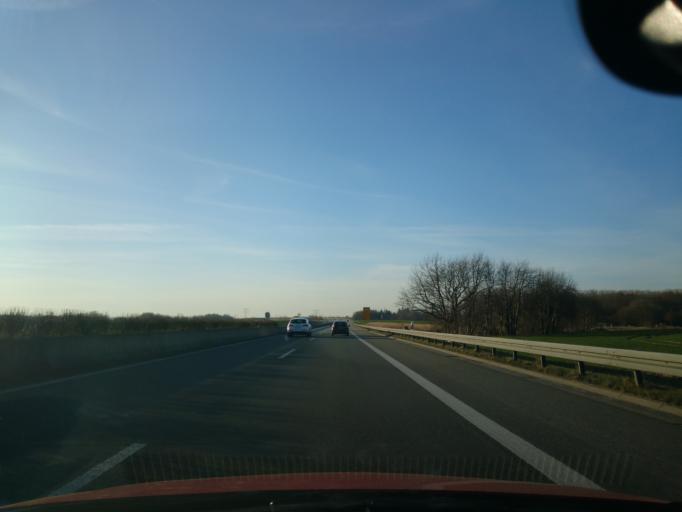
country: DE
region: Mecklenburg-Vorpommern
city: Zarrendorf
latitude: 54.2466
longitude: 13.1333
